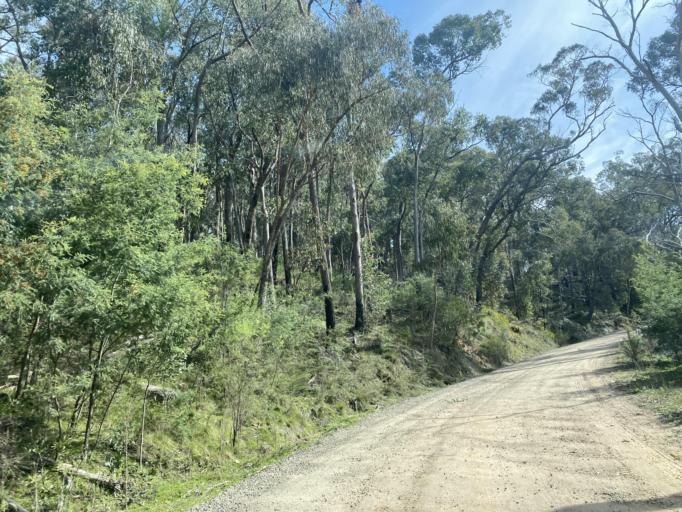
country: AU
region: Victoria
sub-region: Mansfield
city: Mansfield
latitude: -36.8428
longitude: 146.1685
